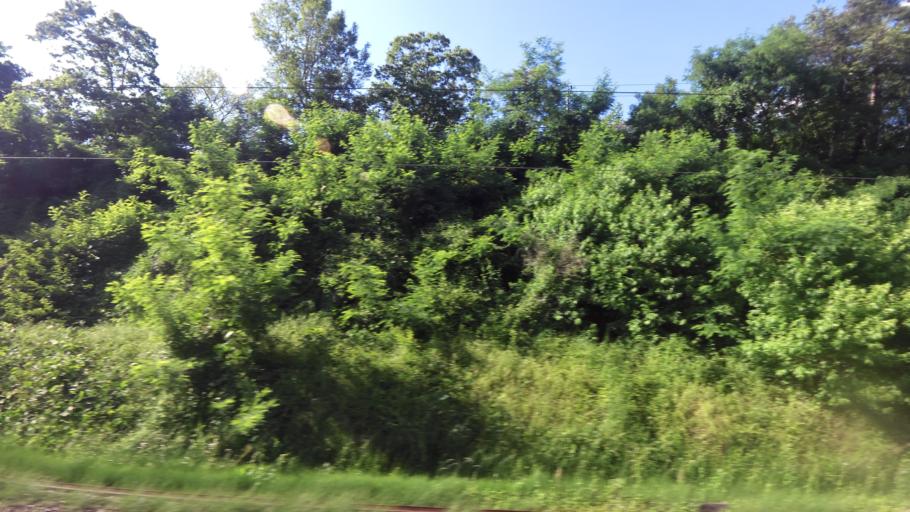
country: KR
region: Gyeongsangbuk-do
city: Waegwan
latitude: 35.9655
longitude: 128.4647
